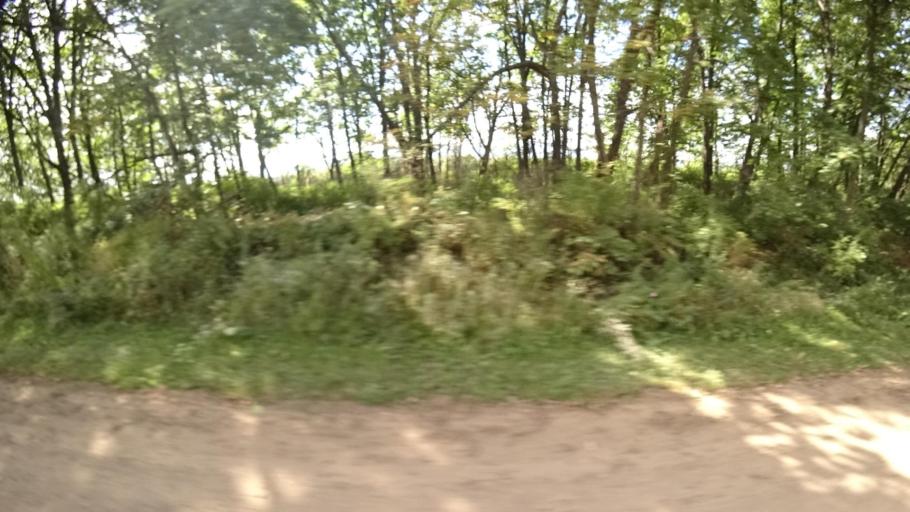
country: RU
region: Primorskiy
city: Yakovlevka
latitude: 44.4133
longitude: 133.5699
